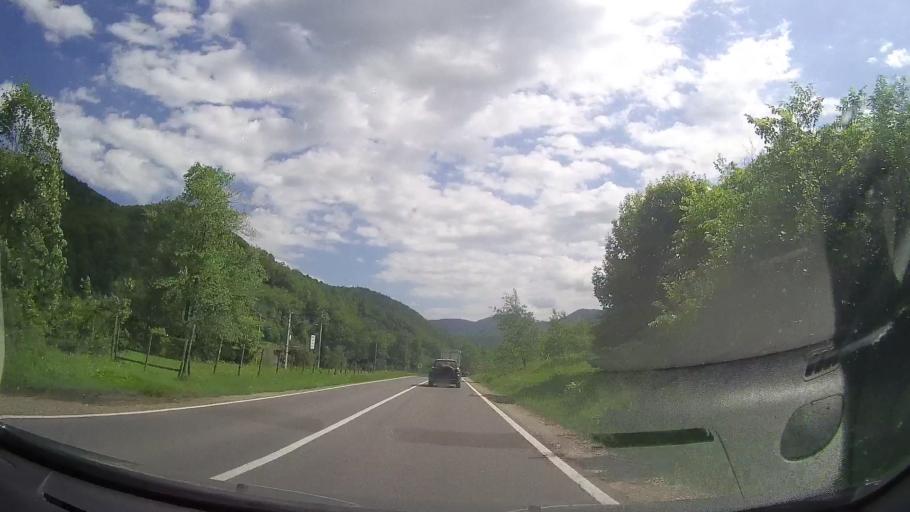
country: RO
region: Prahova
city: Maneciu
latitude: 45.3910
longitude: 25.9307
